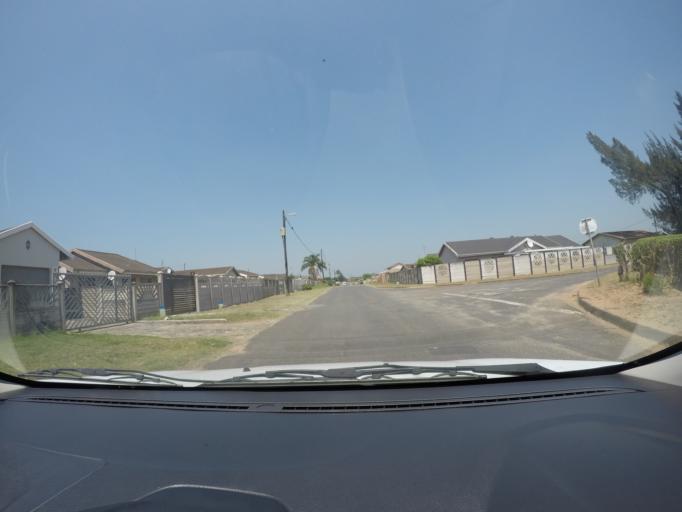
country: ZA
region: KwaZulu-Natal
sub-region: uThungulu District Municipality
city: eSikhawini
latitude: -28.8709
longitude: 31.9227
